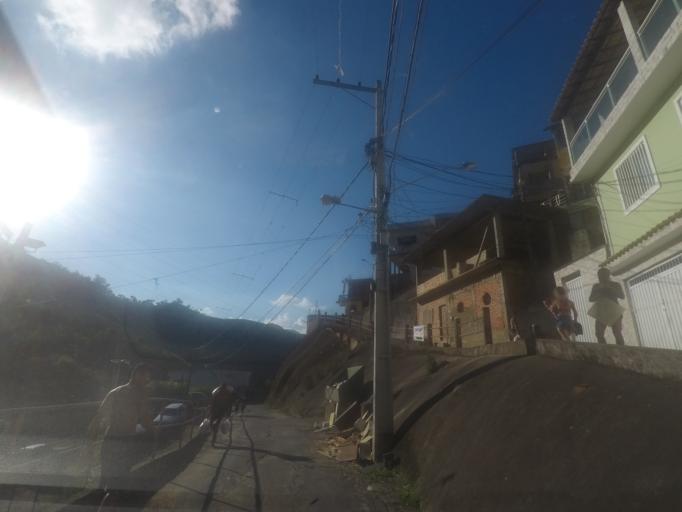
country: BR
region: Rio de Janeiro
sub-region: Petropolis
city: Petropolis
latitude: -22.4998
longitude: -43.1460
